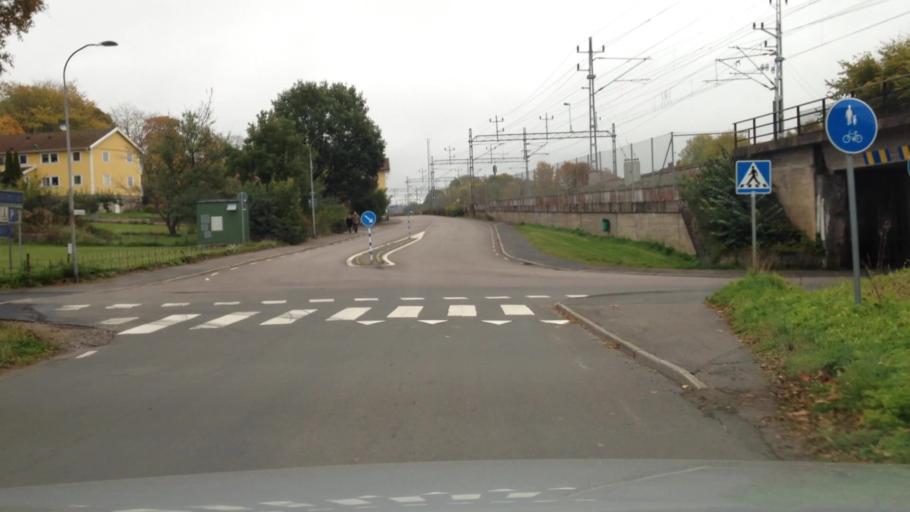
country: SE
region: Vaestra Goetaland
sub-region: Falkopings Kommun
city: Akarp
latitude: 58.2722
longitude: 13.7104
